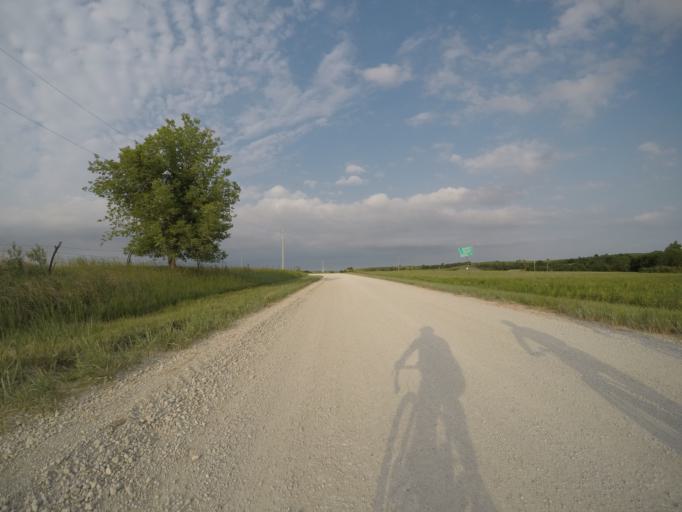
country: US
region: Kansas
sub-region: Wabaunsee County
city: Alma
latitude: 39.1014
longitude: -96.3474
